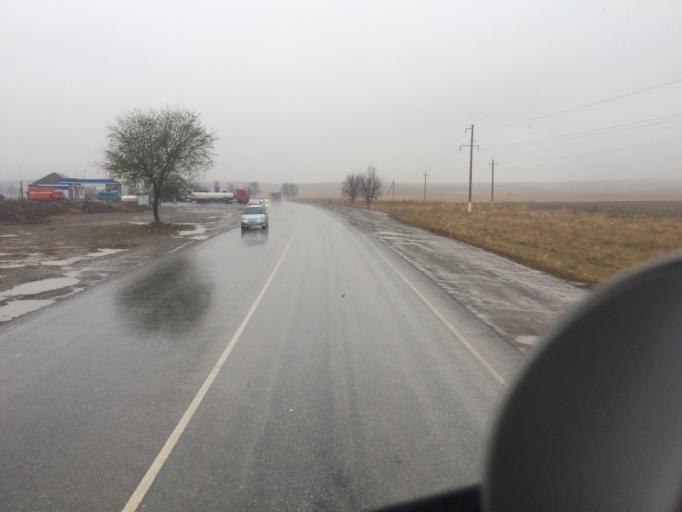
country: KG
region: Chuy
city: Kant
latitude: 43.0031
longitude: 74.8641
